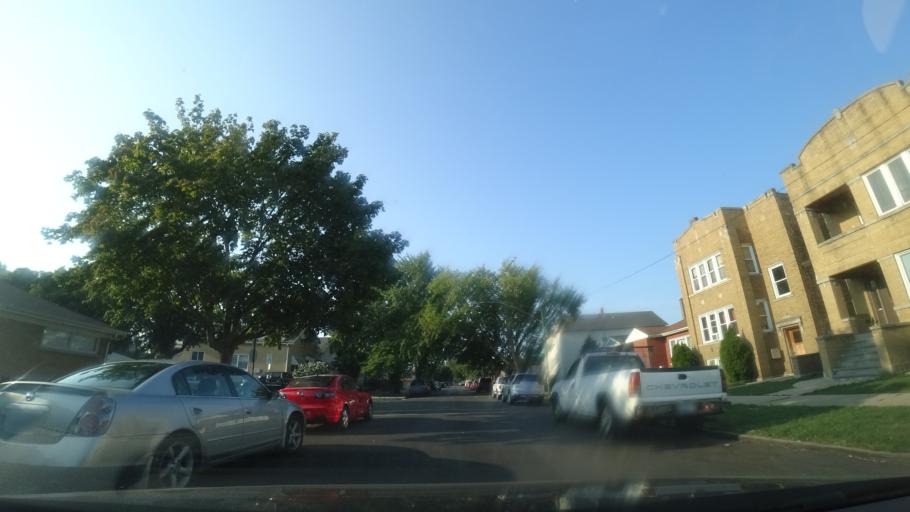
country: US
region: Illinois
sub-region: Cook County
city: Elmwood Park
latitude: 41.9222
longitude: -87.7781
